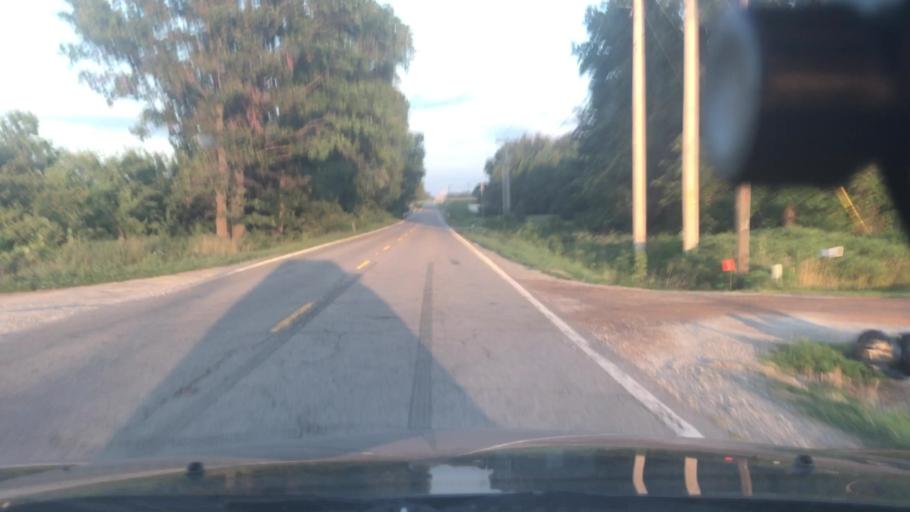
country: US
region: Illinois
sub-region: Washington County
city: Okawville
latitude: 38.4157
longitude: -89.5370
